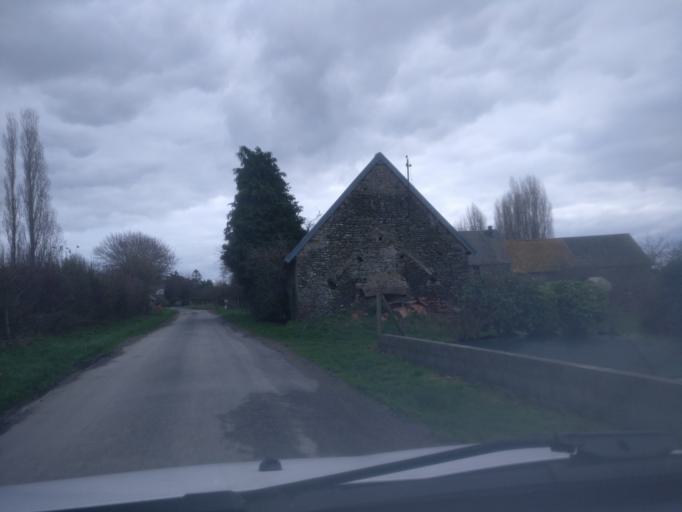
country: FR
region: Lower Normandy
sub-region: Departement de la Manche
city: Marcey-les-Greves
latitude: 48.6711
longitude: -1.4147
